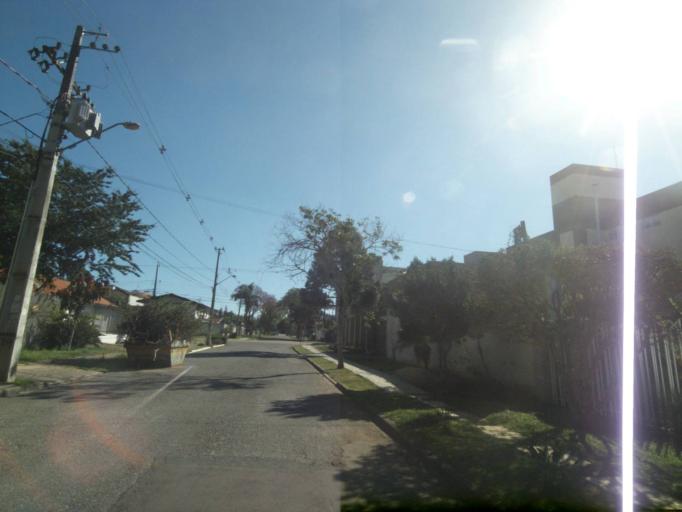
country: BR
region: Parana
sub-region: Curitiba
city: Curitiba
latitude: -25.3932
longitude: -49.2336
